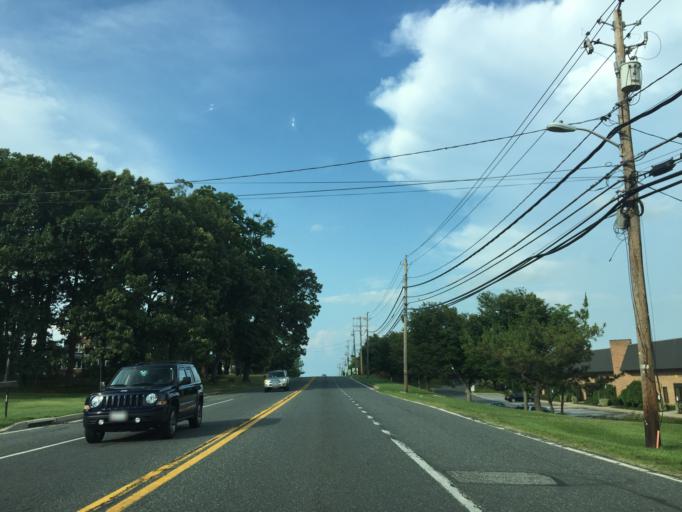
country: US
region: Maryland
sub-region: Baltimore County
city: Rossville
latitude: 39.3513
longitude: -76.4669
